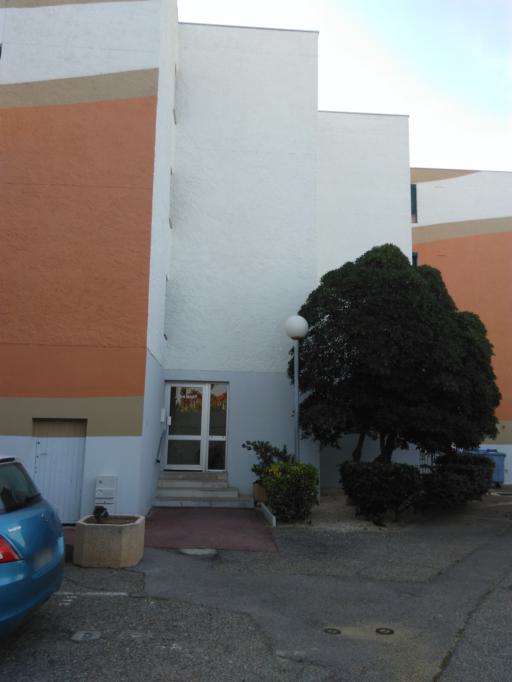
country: FR
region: Languedoc-Roussillon
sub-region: Departement des Pyrenees-Orientales
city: Le Barcares
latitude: 42.7991
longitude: 3.0371
